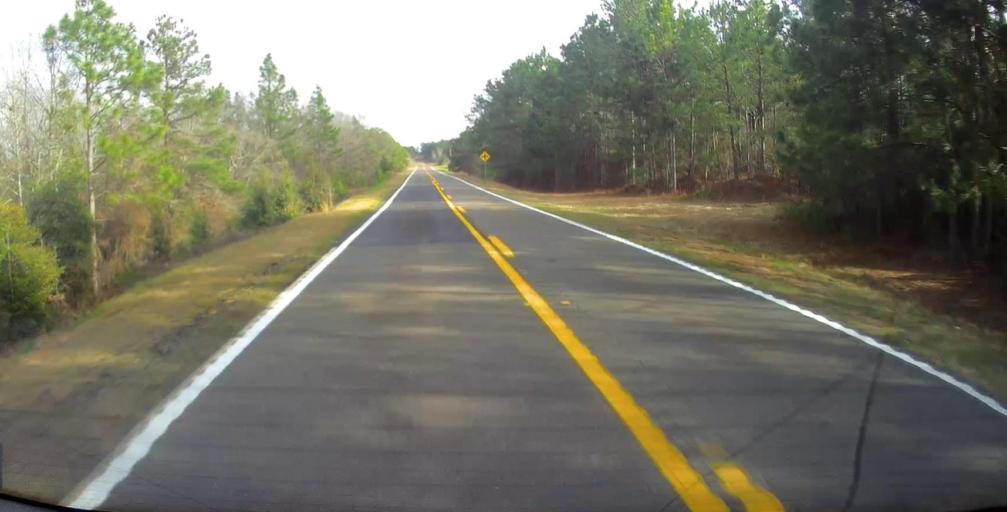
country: US
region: Georgia
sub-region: Marion County
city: Buena Vista
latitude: 32.4425
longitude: -84.5144
